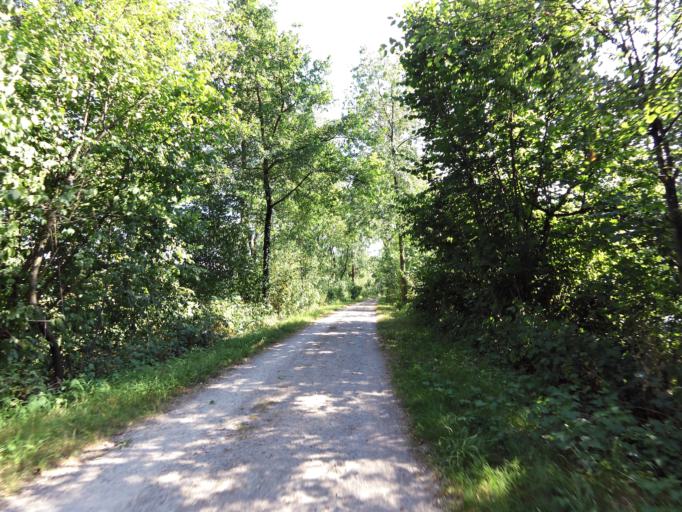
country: CH
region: Aargau
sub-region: Bezirk Lenzburg
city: Niederlenz
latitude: 47.4210
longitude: 8.1639
